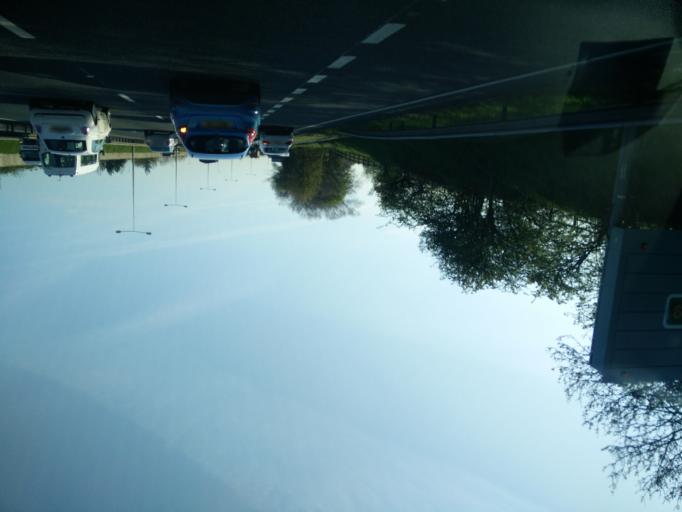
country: GB
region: England
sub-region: Stockton-on-Tees
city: Billingham
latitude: 54.5855
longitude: -1.2993
